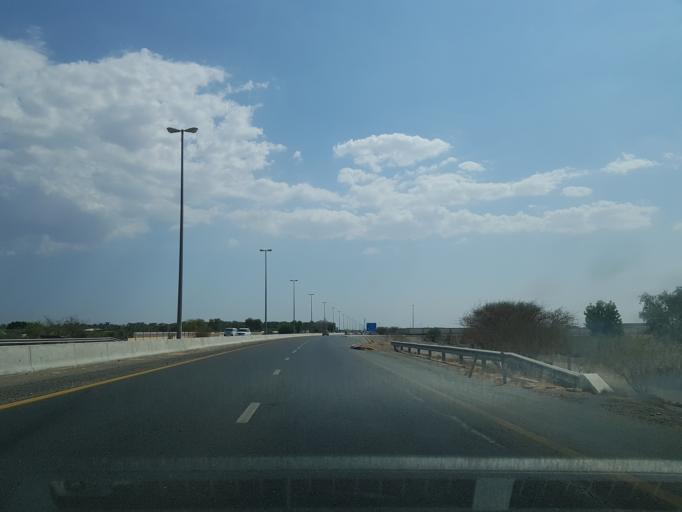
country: AE
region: Ash Shariqah
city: Adh Dhayd
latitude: 25.2387
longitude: 55.9160
